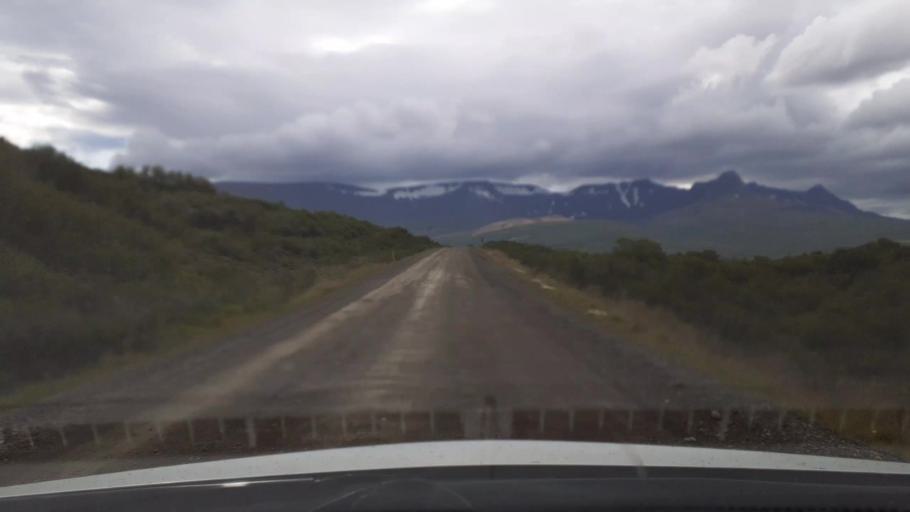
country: IS
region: West
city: Borgarnes
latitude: 64.5556
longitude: -21.6235
